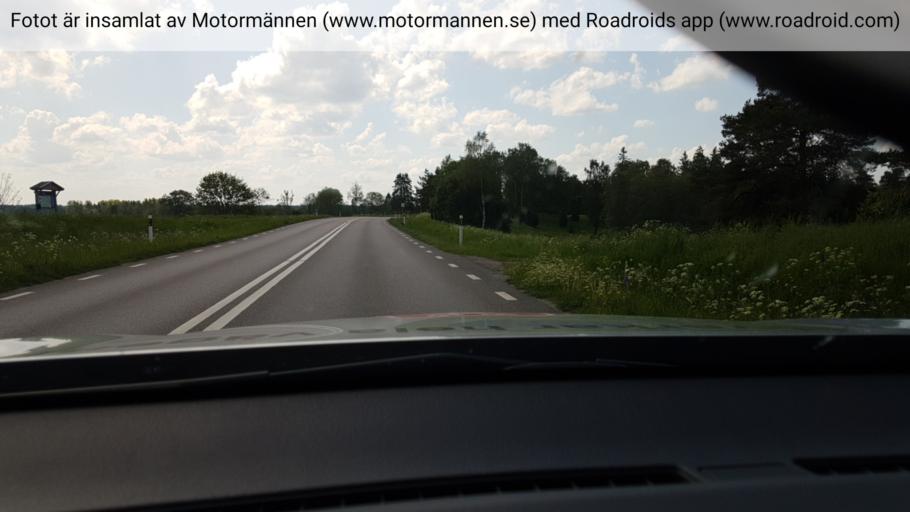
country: SE
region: Vaestra Goetaland
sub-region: Falkopings Kommun
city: Falkoeping
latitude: 58.0155
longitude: 13.5725
